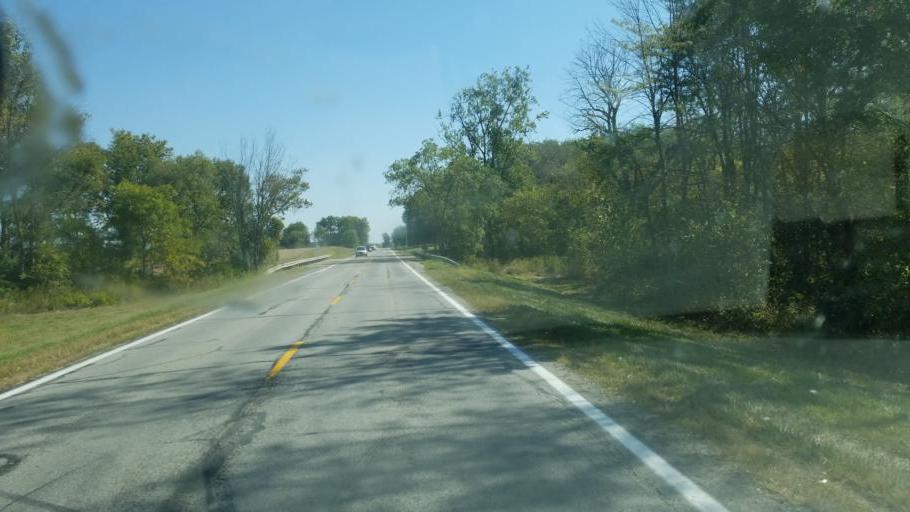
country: US
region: Ohio
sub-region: Wyandot County
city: Upper Sandusky
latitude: 40.6436
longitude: -83.3114
